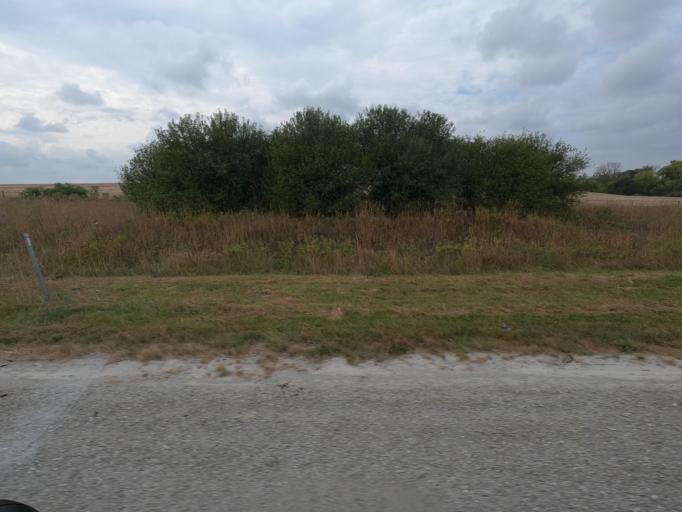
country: US
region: Iowa
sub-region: Jasper County
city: Monroe
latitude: 41.5241
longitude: -93.1305
